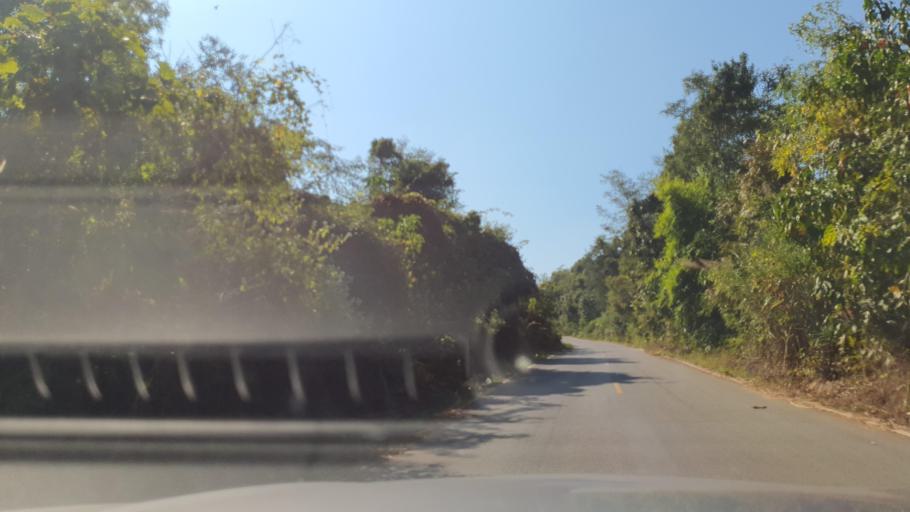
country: TH
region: Nan
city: Pua
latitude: 19.1595
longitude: 100.9066
